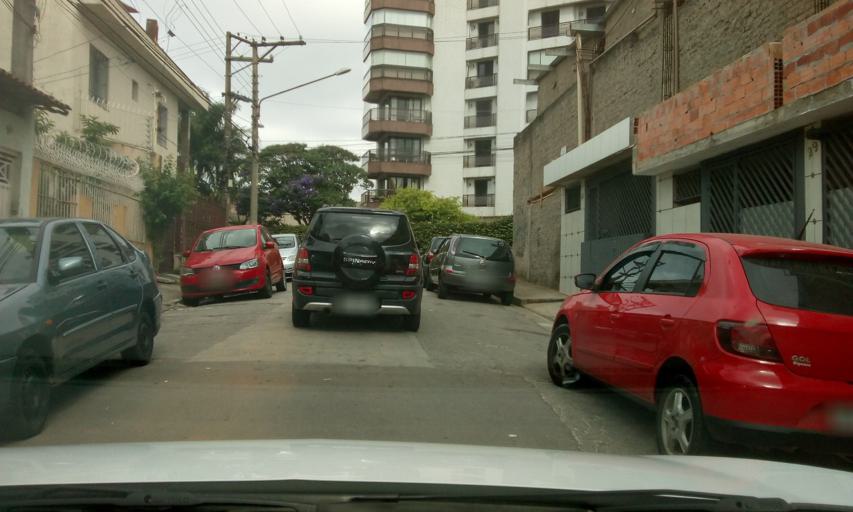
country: BR
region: Sao Paulo
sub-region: Sao Paulo
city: Sao Paulo
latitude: -23.5266
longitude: -46.6163
